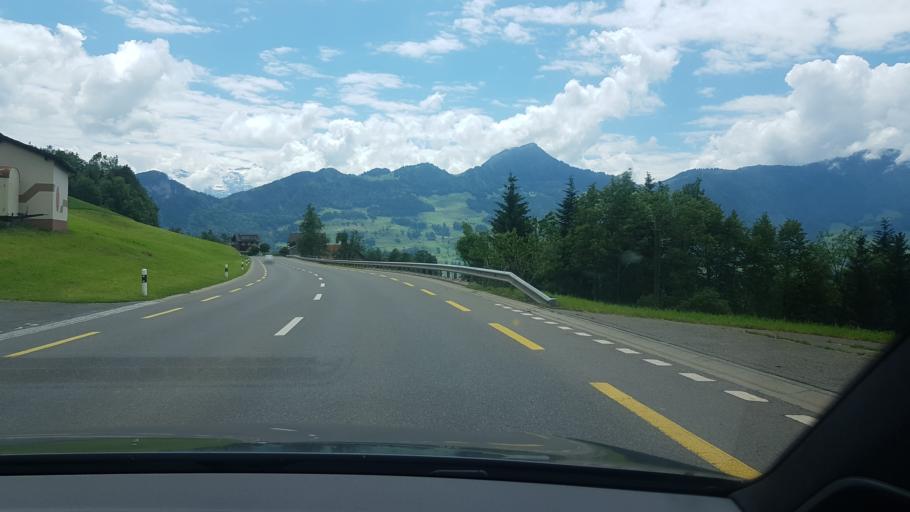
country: CH
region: Schwyz
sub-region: Bezirk Schwyz
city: Steinen
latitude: 47.0640
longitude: 8.6224
